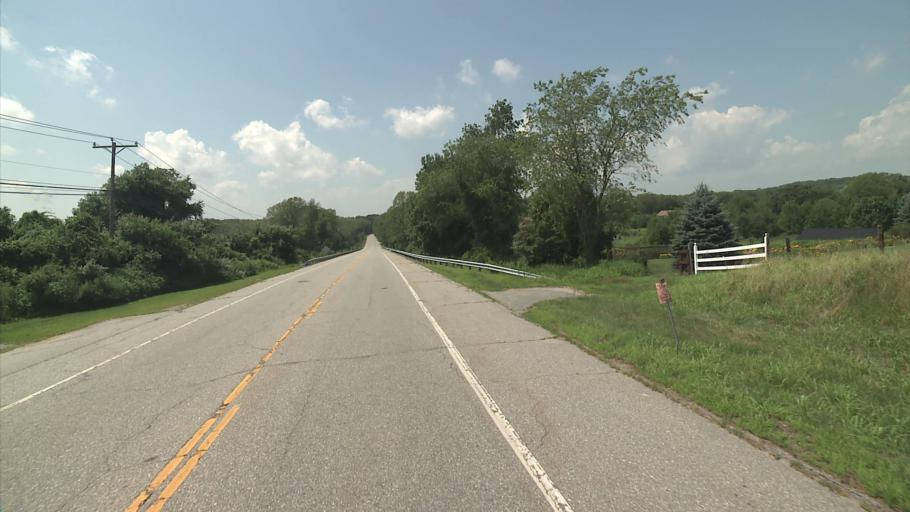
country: US
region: Connecticut
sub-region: New London County
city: Preston City
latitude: 41.5344
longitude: -72.0198
